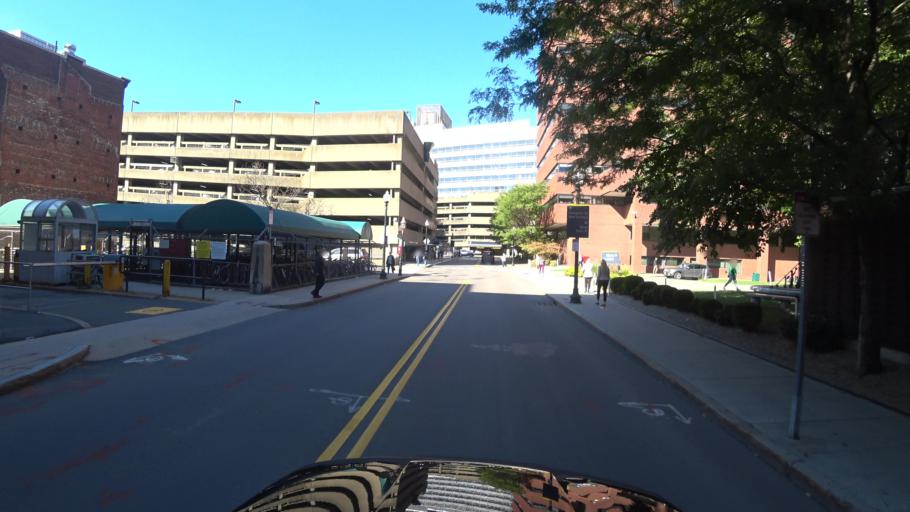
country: US
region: Massachusetts
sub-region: Suffolk County
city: Boston
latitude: 42.3622
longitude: -71.0675
